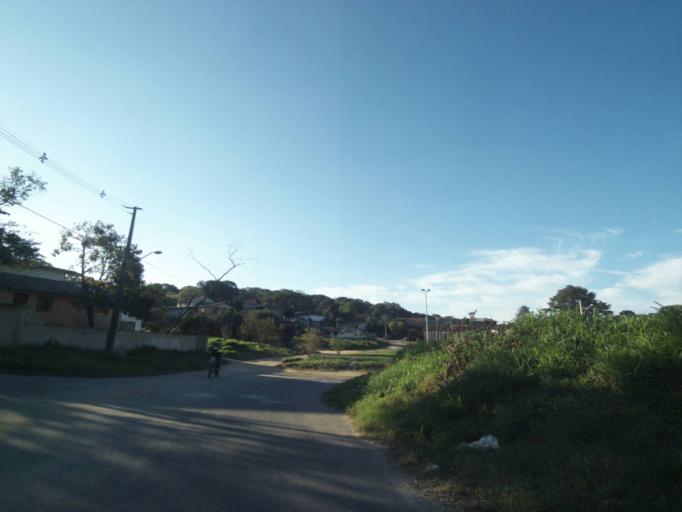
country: BR
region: Parana
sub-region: Curitiba
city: Curitiba
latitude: -25.3723
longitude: -49.2521
